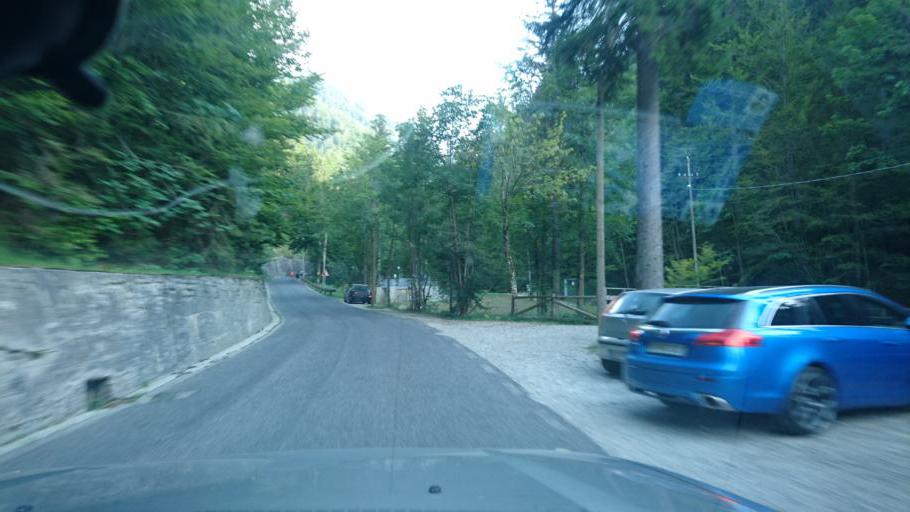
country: AT
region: Carinthia
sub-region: Politischer Bezirk Villach Land
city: Arnoldstein
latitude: 46.4874
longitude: 13.6730
